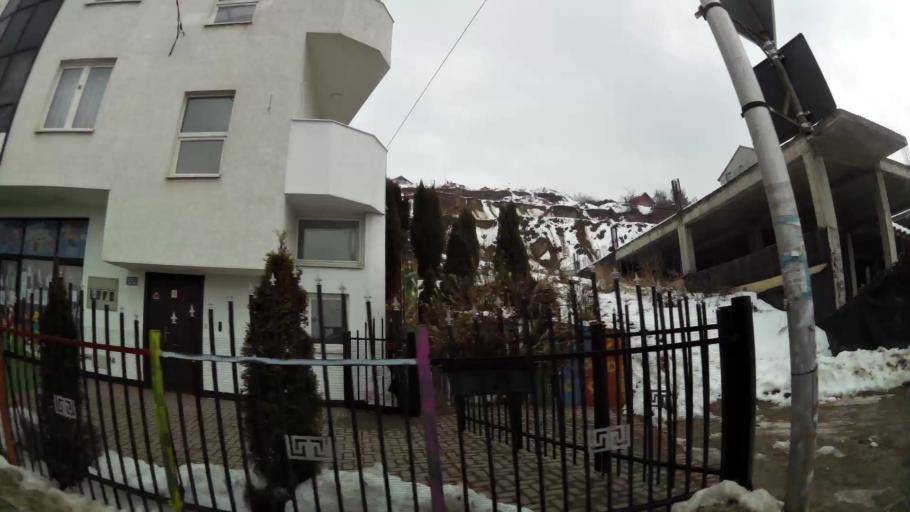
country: XK
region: Pristina
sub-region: Komuna e Prishtines
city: Pristina
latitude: 42.6756
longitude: 21.1746
